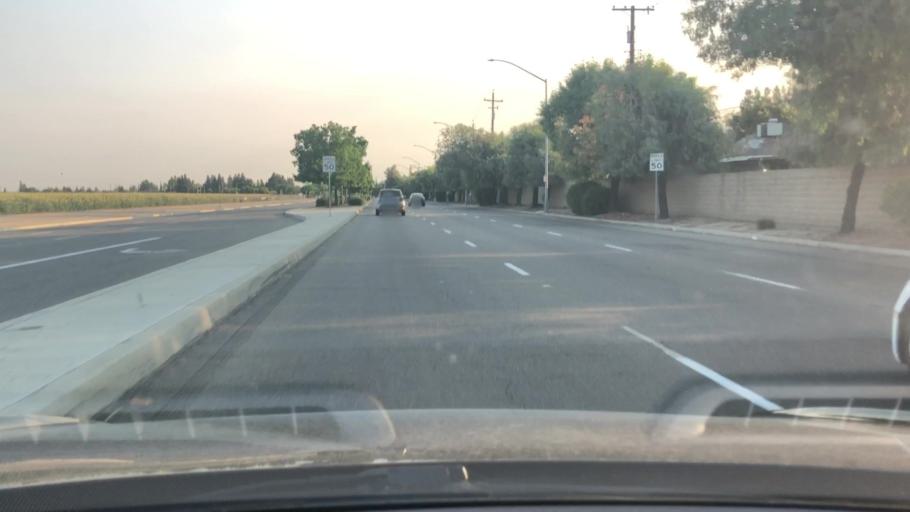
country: US
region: California
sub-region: Fresno County
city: Clovis
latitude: 36.8164
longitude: -119.7273
